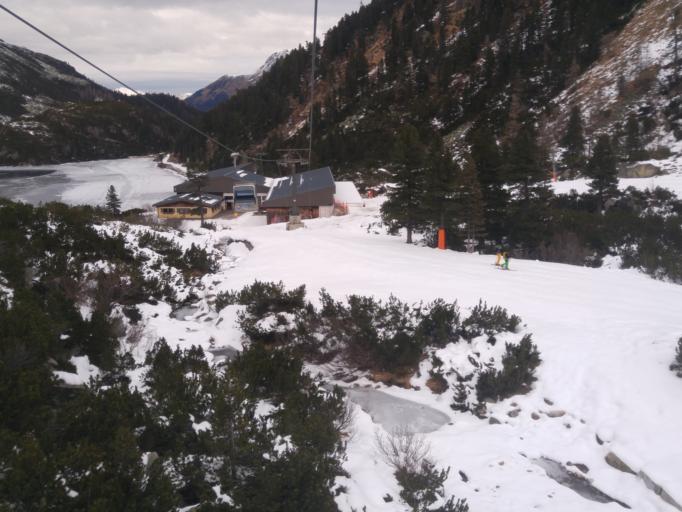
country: AT
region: Salzburg
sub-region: Politischer Bezirk Zell am See
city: Niedernsill
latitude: 47.1554
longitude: 12.6240
